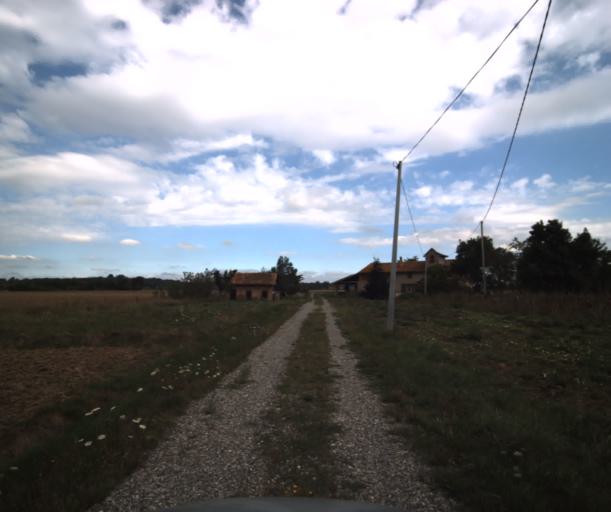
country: FR
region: Midi-Pyrenees
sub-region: Departement de la Haute-Garonne
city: Lherm
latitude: 43.3940
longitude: 1.2300
